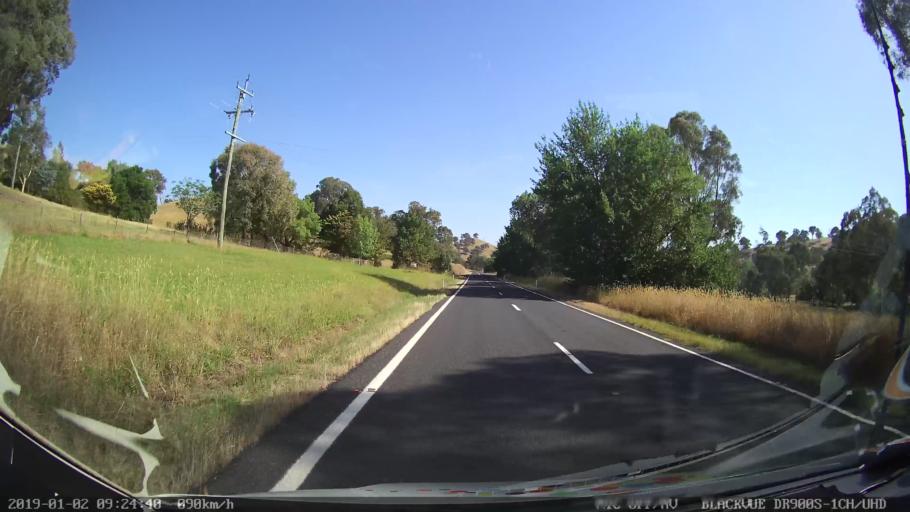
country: AU
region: New South Wales
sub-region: Tumut Shire
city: Tumut
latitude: -35.3740
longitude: 148.2917
